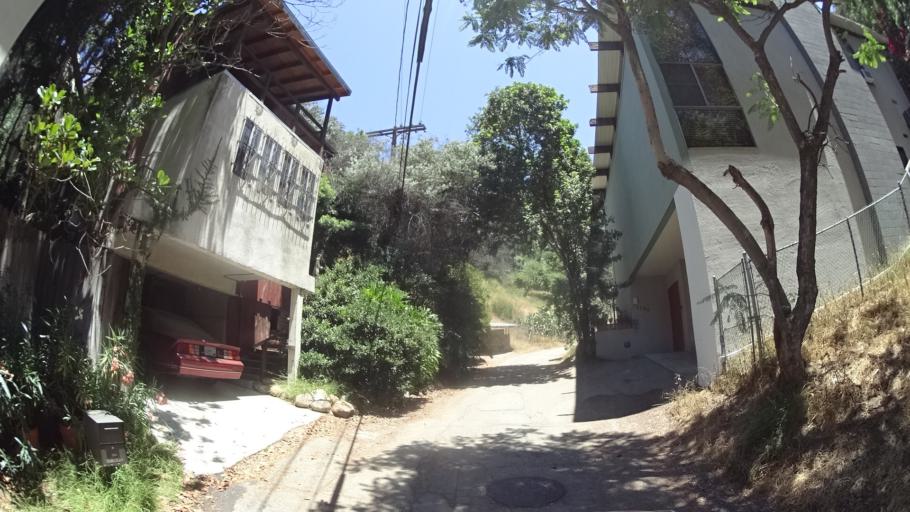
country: US
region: California
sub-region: Los Angeles County
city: Universal City
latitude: 34.1183
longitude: -118.3711
